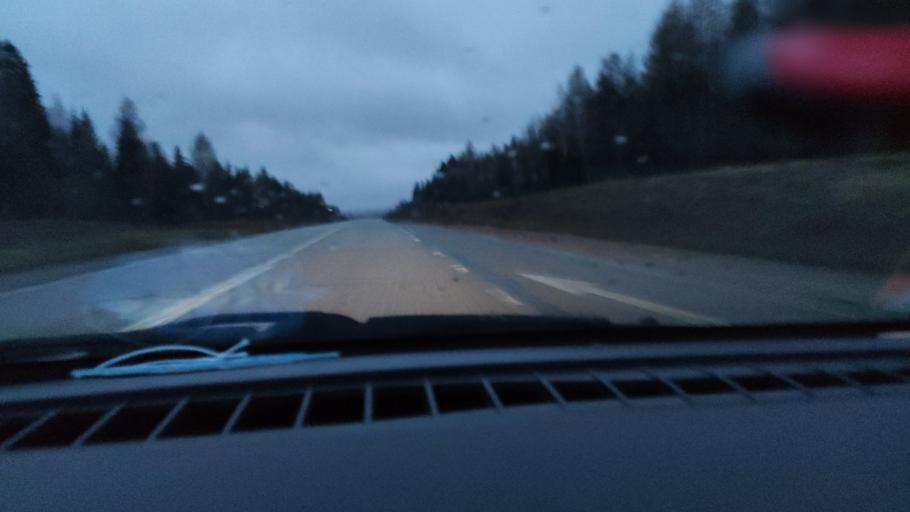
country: RU
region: Udmurtiya
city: Mozhga
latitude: 56.3338
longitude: 52.3015
